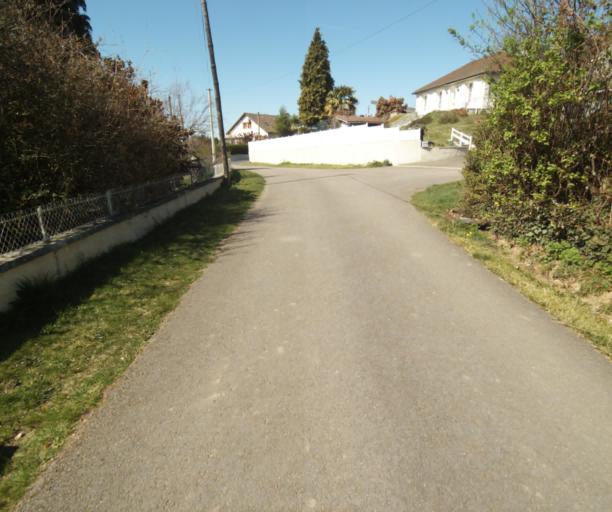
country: FR
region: Limousin
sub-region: Departement de la Correze
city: Saint-Mexant
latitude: 45.2791
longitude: 1.6636
